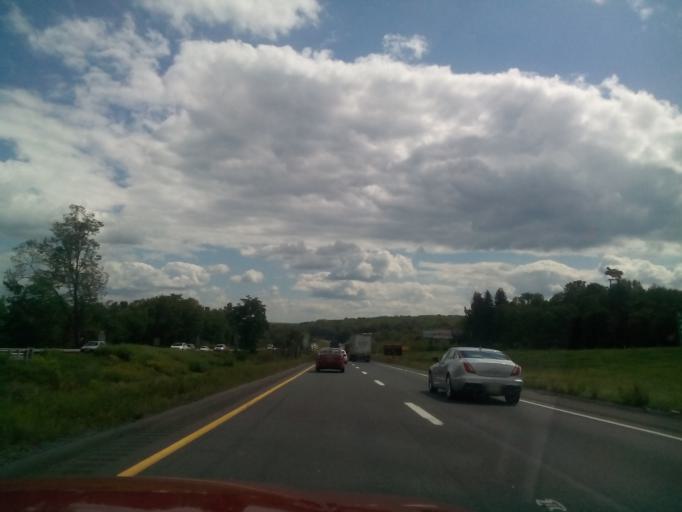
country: US
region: Pennsylvania
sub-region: Monroe County
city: Tannersville
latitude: 41.0388
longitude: -75.3125
